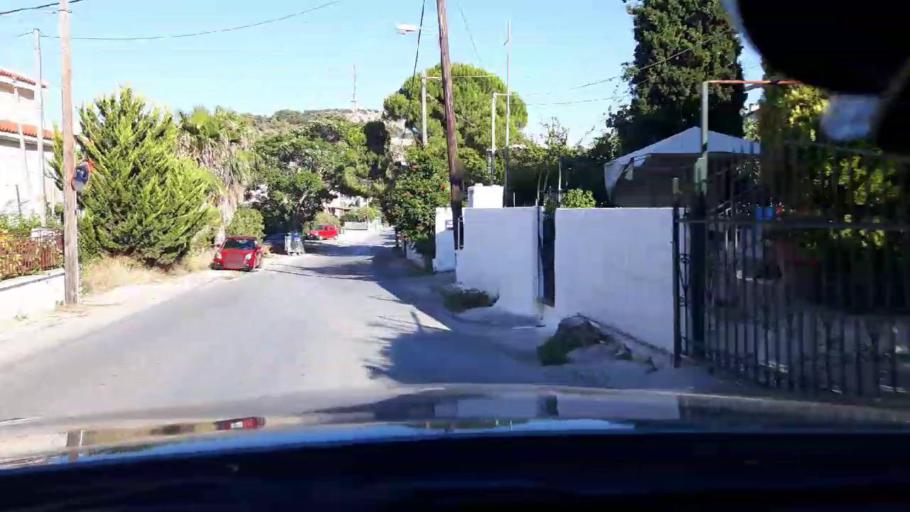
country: GR
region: Attica
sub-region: Nomarchia Anatolikis Attikis
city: Limin Mesoyaias
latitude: 37.8822
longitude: 24.0028
